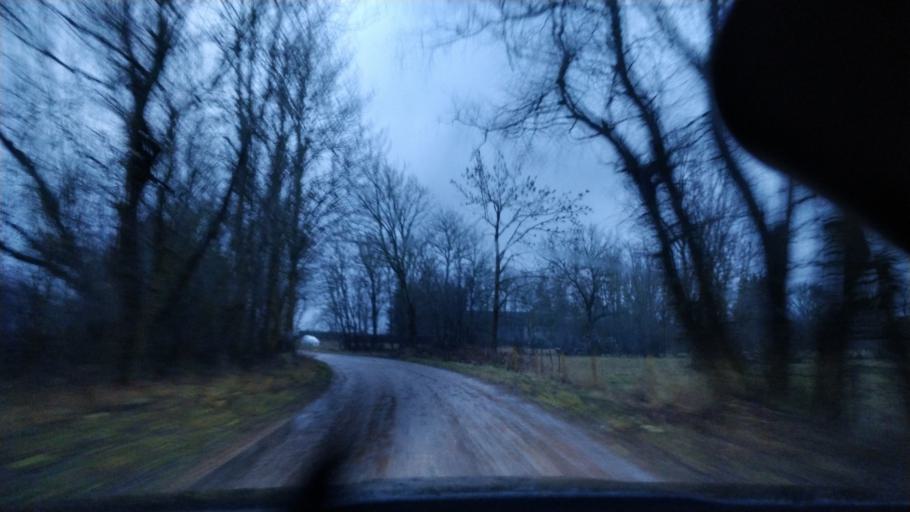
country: EE
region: Laeaene
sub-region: Lihula vald
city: Lihula
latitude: 58.8494
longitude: 23.9835
